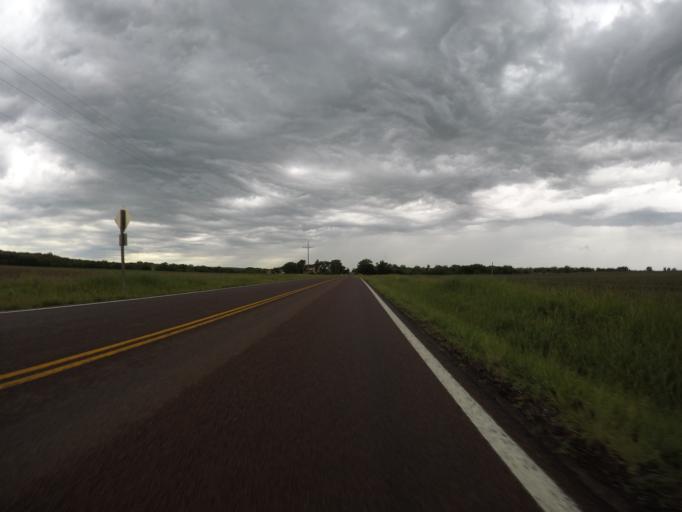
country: US
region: Kansas
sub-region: Shawnee County
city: Rossville
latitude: 38.9573
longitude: -96.0243
